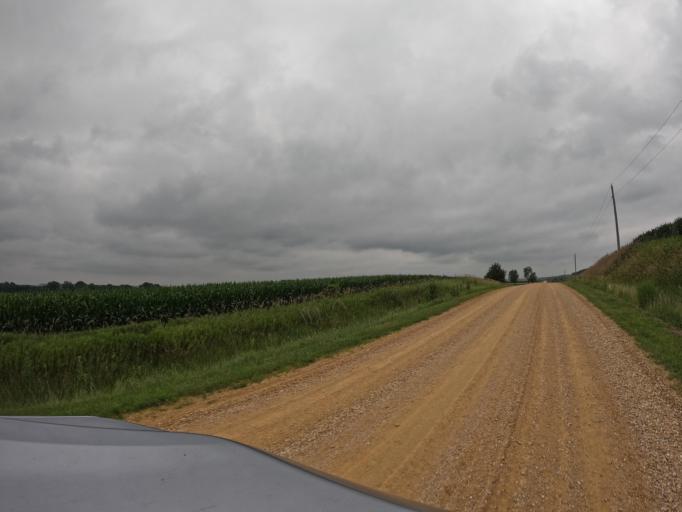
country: US
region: Illinois
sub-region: Carroll County
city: Savanna
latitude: 41.9825
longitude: -90.1861
